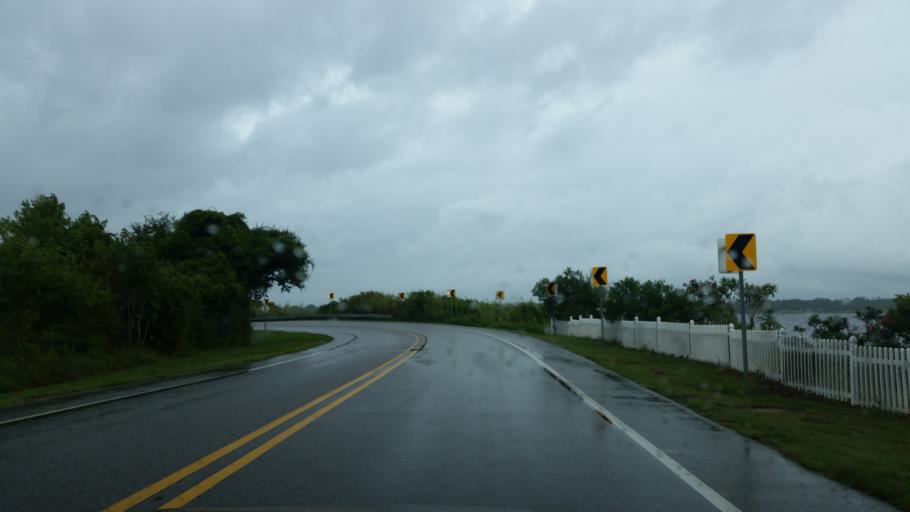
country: US
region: Alabama
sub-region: Baldwin County
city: Gulf Shores
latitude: 30.2538
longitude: -87.6676
